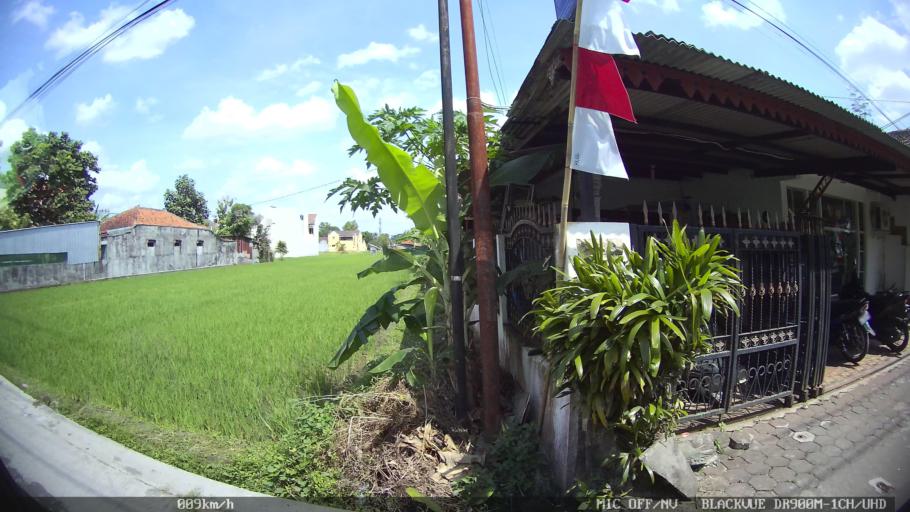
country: ID
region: Daerah Istimewa Yogyakarta
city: Yogyakarta
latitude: -7.8283
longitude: 110.3779
